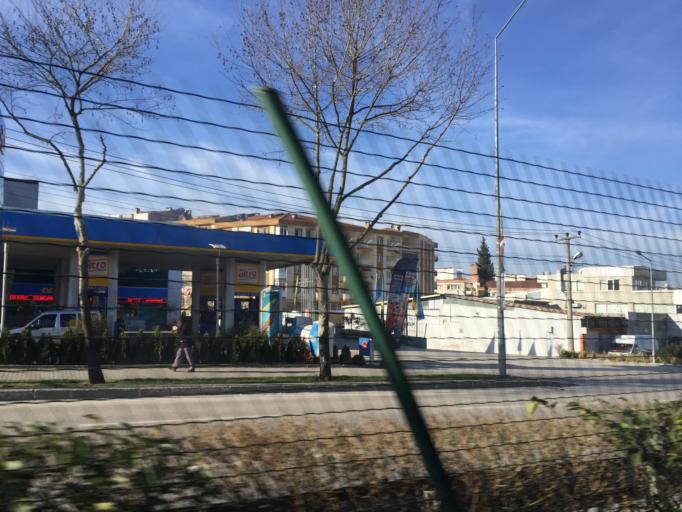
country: TR
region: Bursa
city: Niluefer
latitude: 40.2350
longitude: 28.9781
